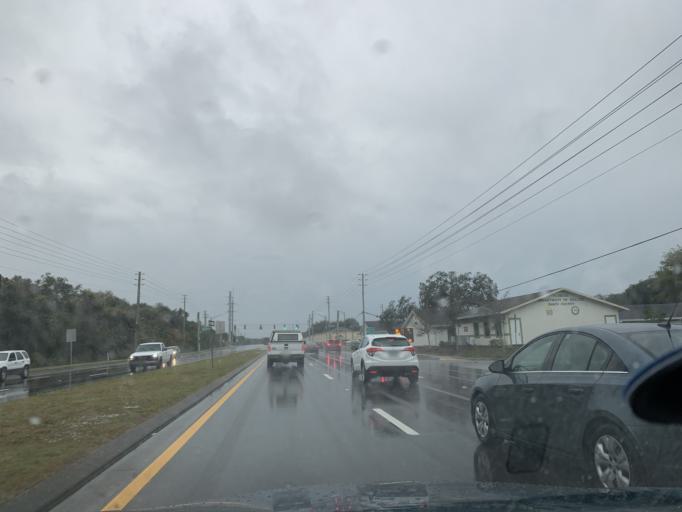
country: US
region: Florida
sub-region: Pasco County
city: Bayonet Point
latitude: 28.3162
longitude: -82.6661
